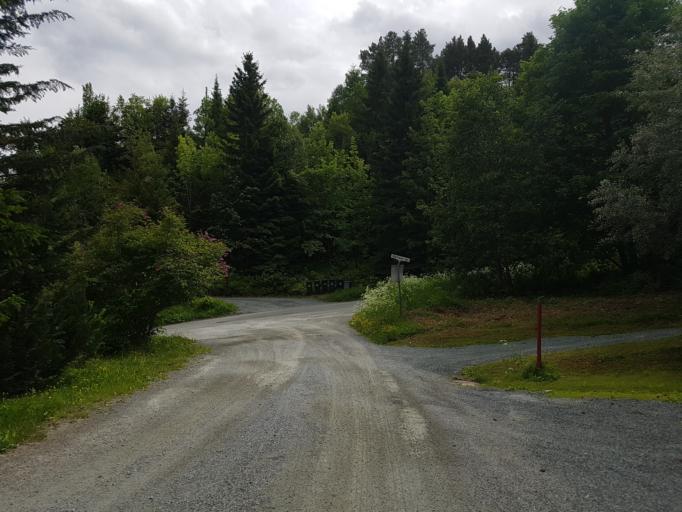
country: NO
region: Sor-Trondelag
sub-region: Trondheim
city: Trondheim
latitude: 63.4256
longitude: 10.3429
